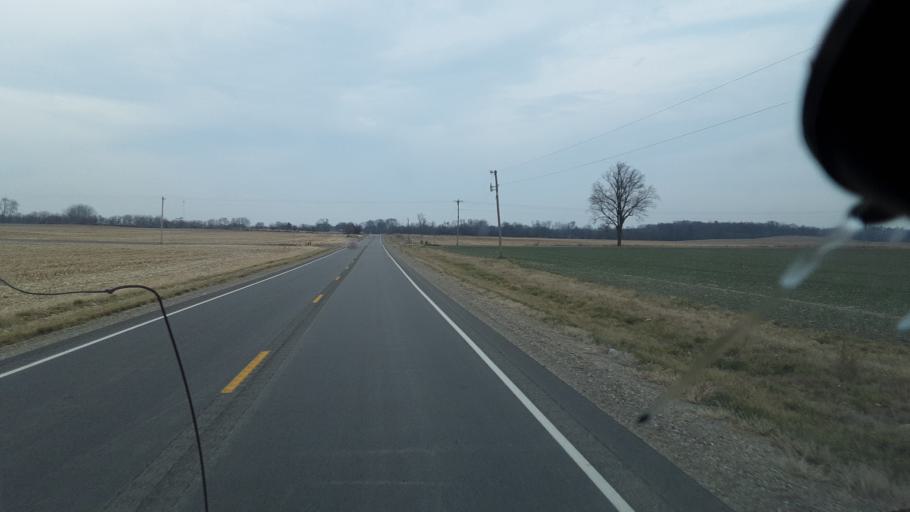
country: US
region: Indiana
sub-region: Steuben County
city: Angola
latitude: 41.6054
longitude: -85.1693
